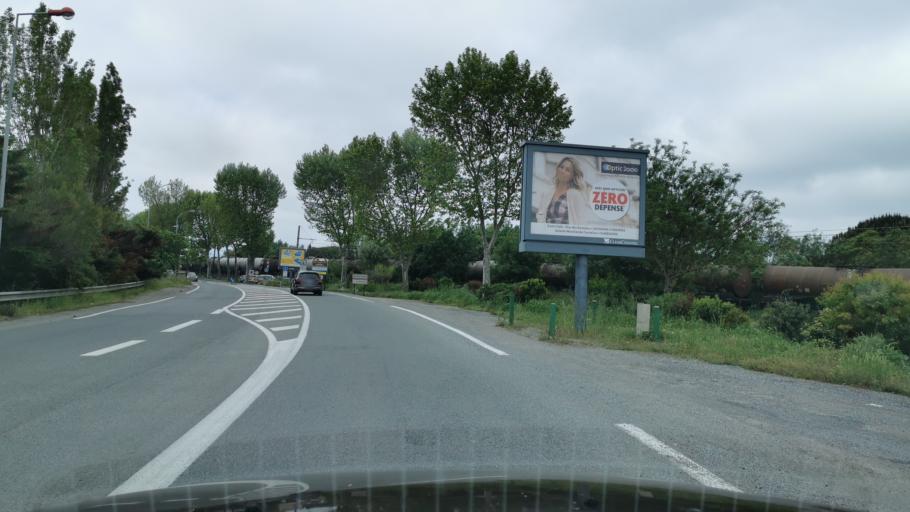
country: FR
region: Languedoc-Roussillon
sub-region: Departement de l'Aude
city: Narbonne
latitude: 43.1993
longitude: 3.0158
